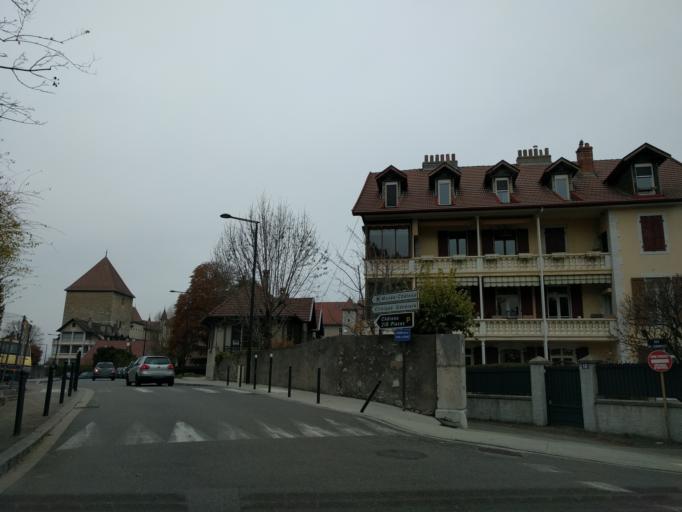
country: FR
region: Rhone-Alpes
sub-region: Departement de la Haute-Savoie
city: Annecy
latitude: 45.8962
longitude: 6.1275
